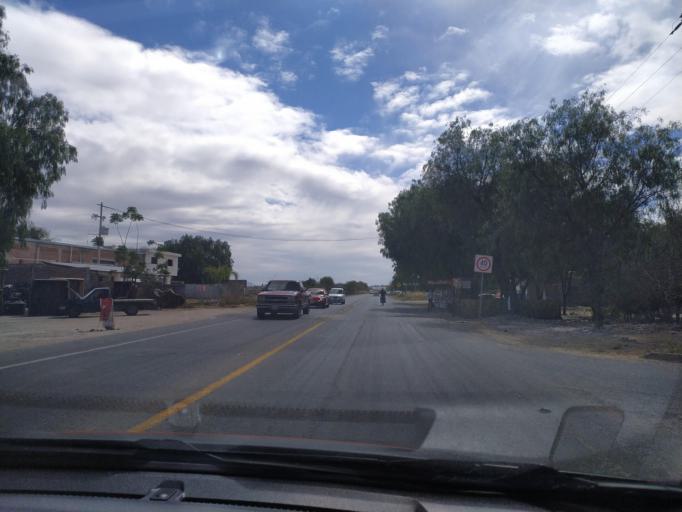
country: LA
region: Oudomxai
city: Muang La
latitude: 21.0156
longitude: 101.8276
